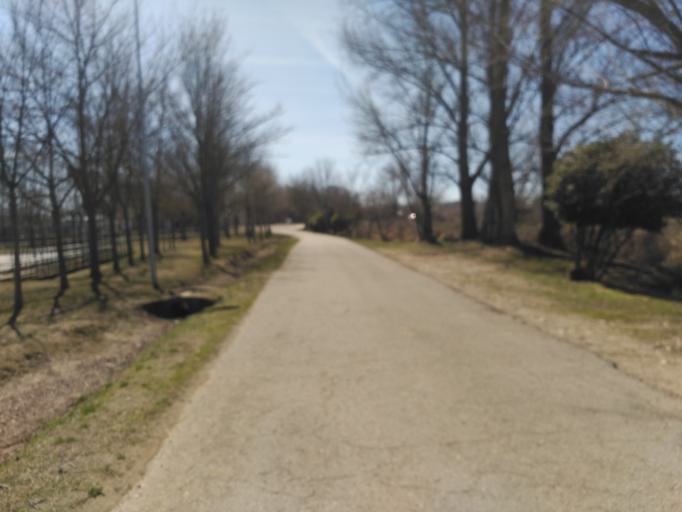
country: ES
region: Castille and Leon
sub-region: Provincia de Leon
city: Hospital de Orbigo
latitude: 42.4376
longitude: -5.8778
